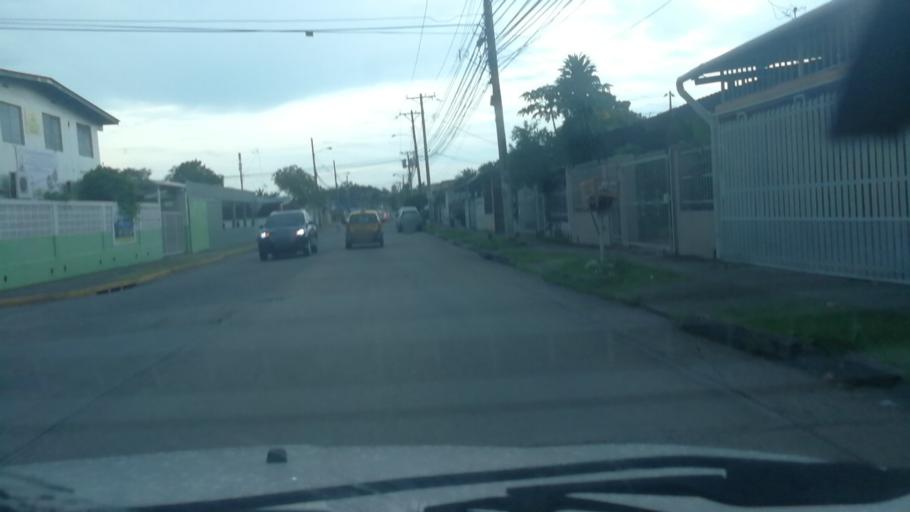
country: PA
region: Panama
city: Tocumen
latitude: 9.0593
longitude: -79.4141
